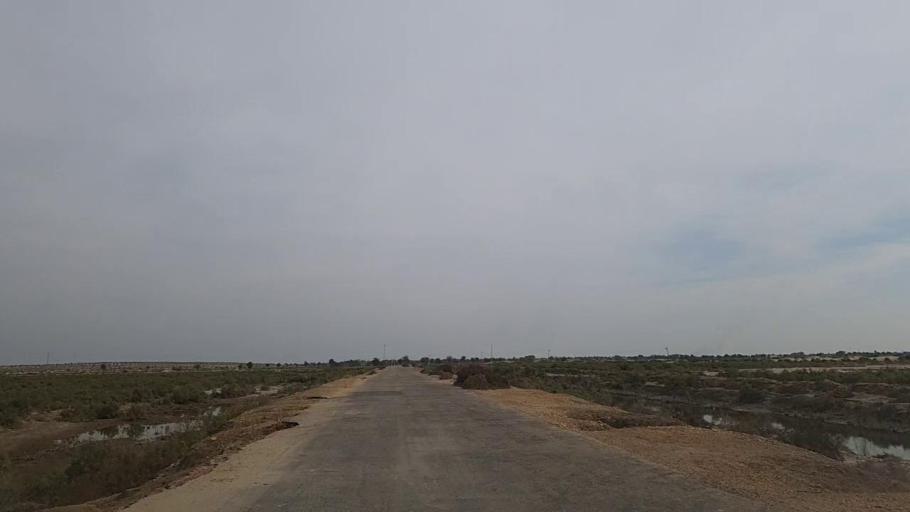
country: PK
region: Sindh
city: Jam Sahib
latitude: 26.4024
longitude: 68.5012
